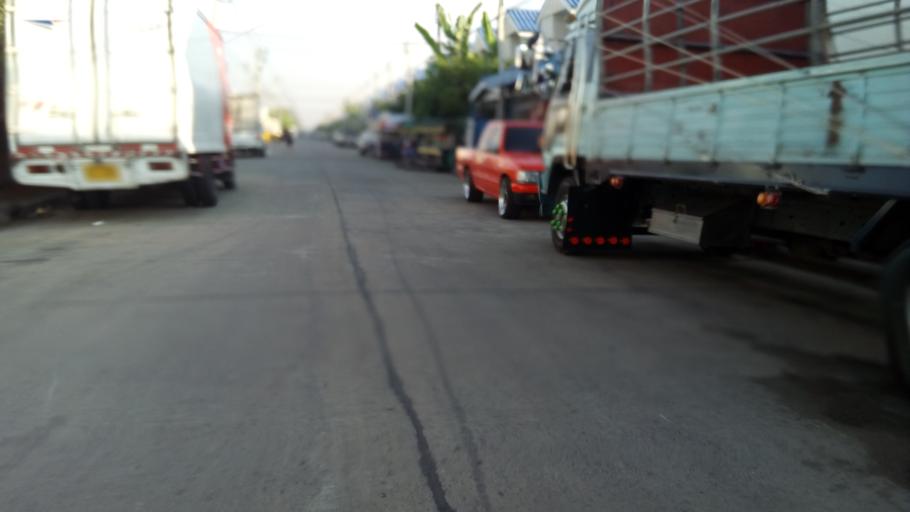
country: TH
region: Pathum Thani
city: Ban Rangsit
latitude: 14.0472
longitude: 100.8410
